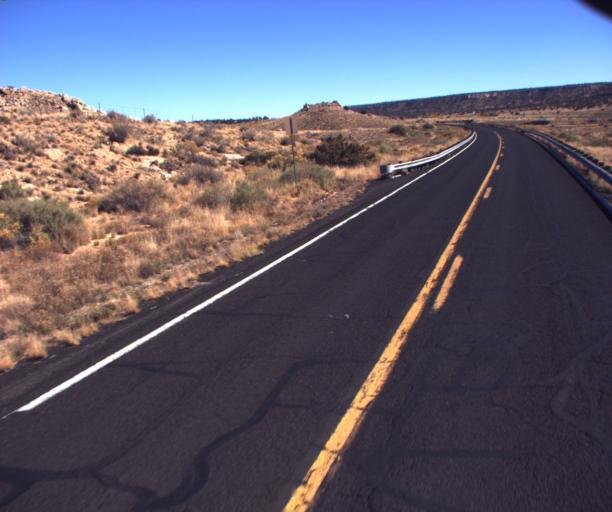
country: US
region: Arizona
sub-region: Navajo County
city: First Mesa
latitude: 35.8298
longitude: -110.2844
